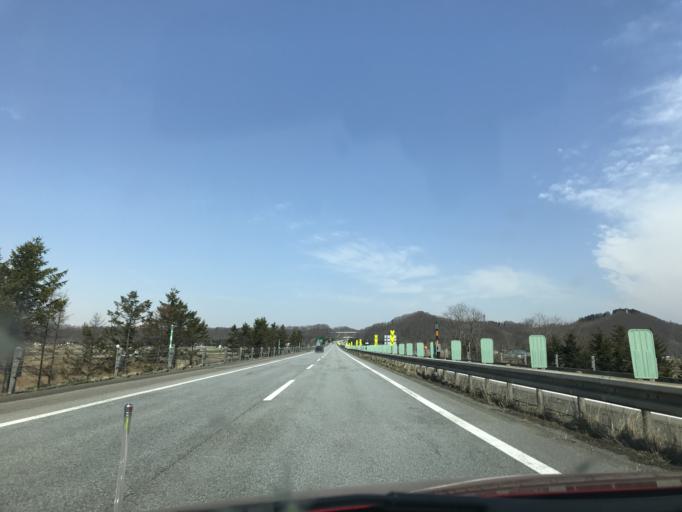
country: JP
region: Hokkaido
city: Iwamizawa
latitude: 43.2333
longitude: 141.8305
